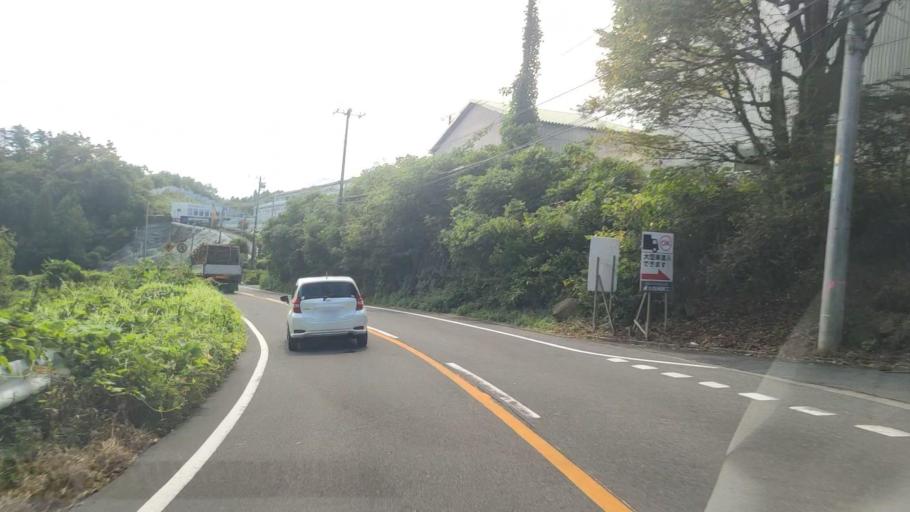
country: JP
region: Gunma
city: Numata
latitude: 36.6280
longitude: 139.0124
